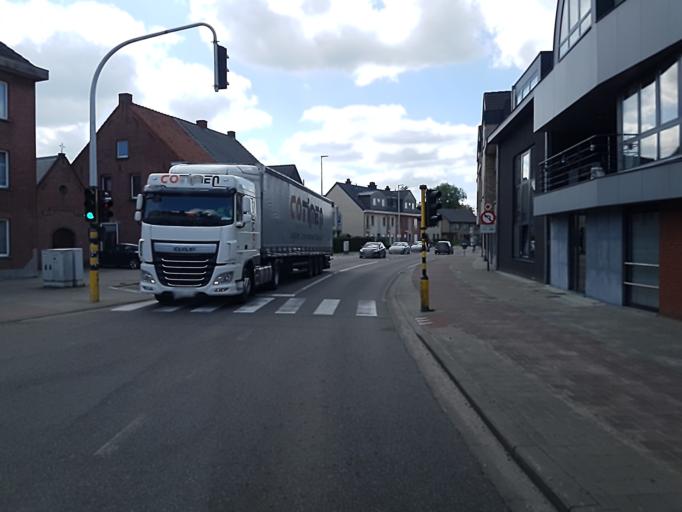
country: BE
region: Flanders
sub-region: Provincie Antwerpen
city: Brecht
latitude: 51.3497
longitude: 4.6752
